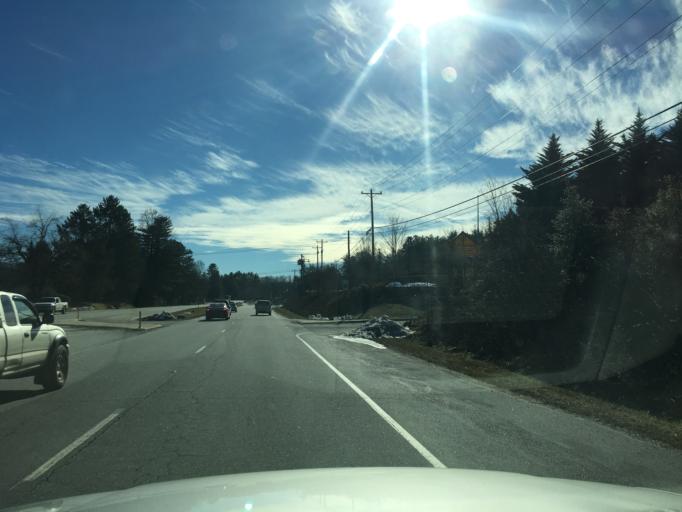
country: US
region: North Carolina
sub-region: Transylvania County
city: Brevard
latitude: 35.2632
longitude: -82.7156
